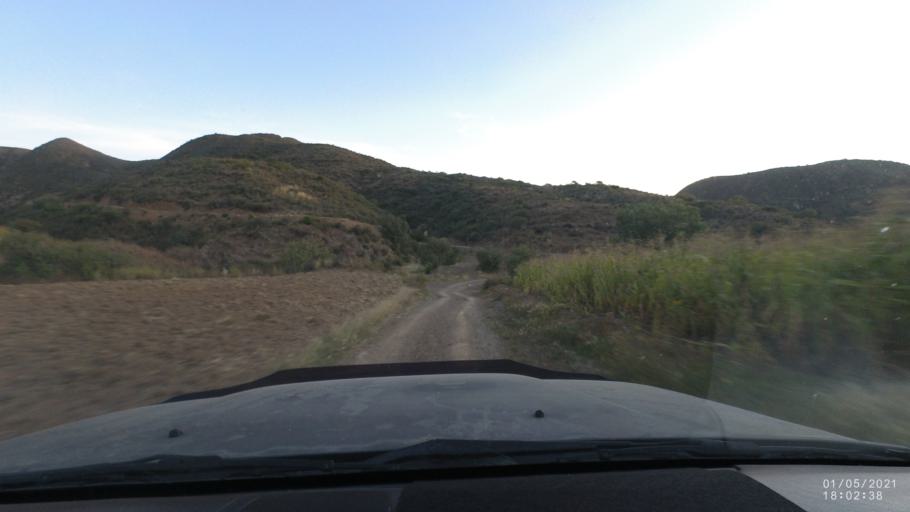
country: BO
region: Cochabamba
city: Capinota
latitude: -17.6886
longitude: -66.1743
